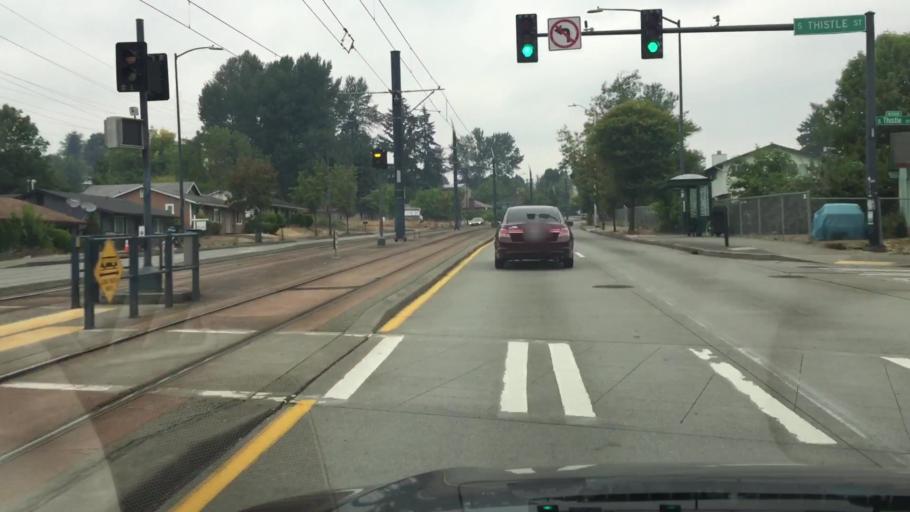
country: US
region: Washington
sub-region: King County
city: Riverton
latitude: 47.5277
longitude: -122.2799
